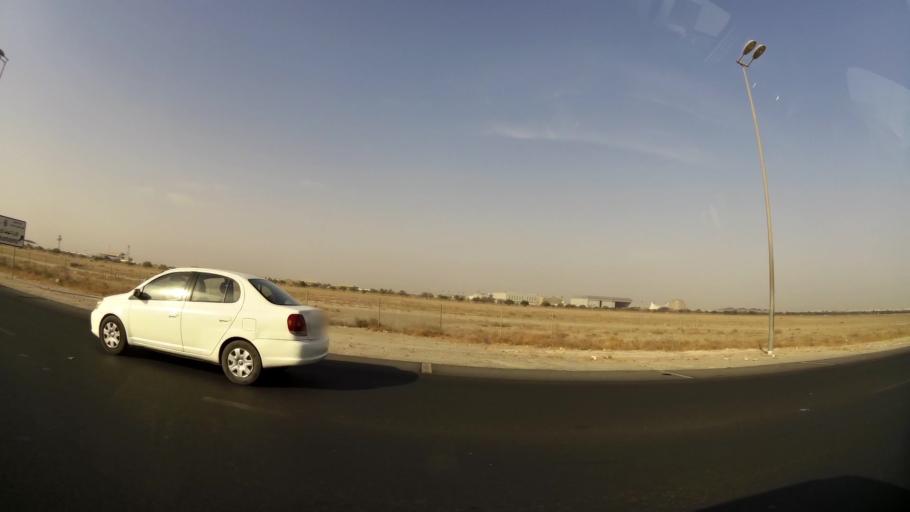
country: KW
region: Al Farwaniyah
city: Janub as Surrah
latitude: 29.2393
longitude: 47.9914
